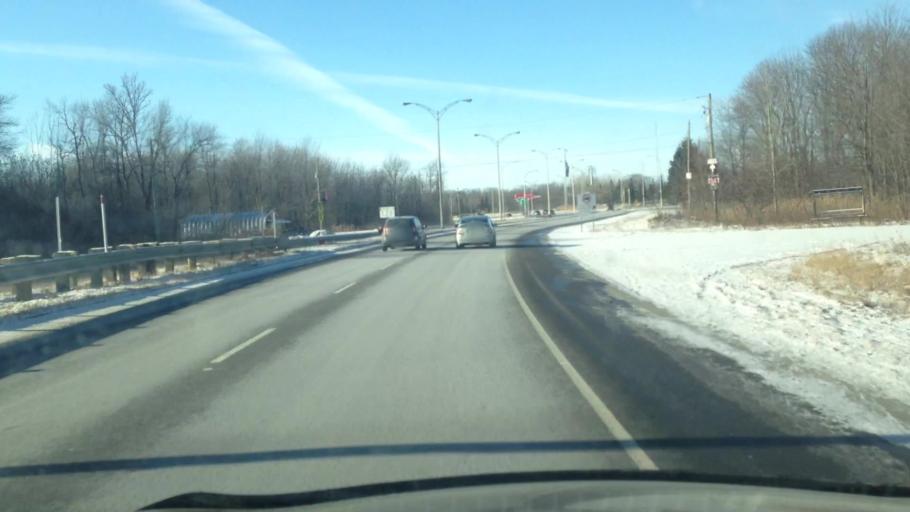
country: CA
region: Quebec
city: Montreal-Ouest
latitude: 45.3992
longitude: -73.6859
